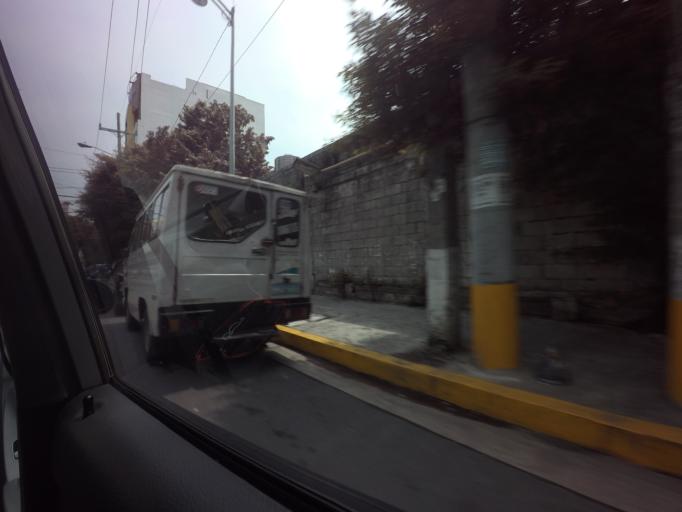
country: PH
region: Metro Manila
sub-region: City of Manila
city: Port Area
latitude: 14.5684
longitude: 120.9935
